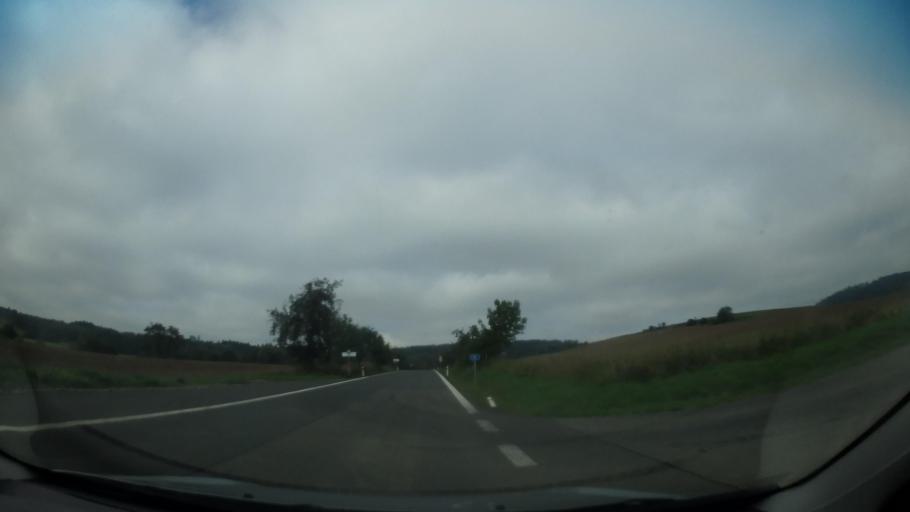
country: CZ
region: Central Bohemia
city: Neveklov
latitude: 49.7537
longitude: 14.5836
